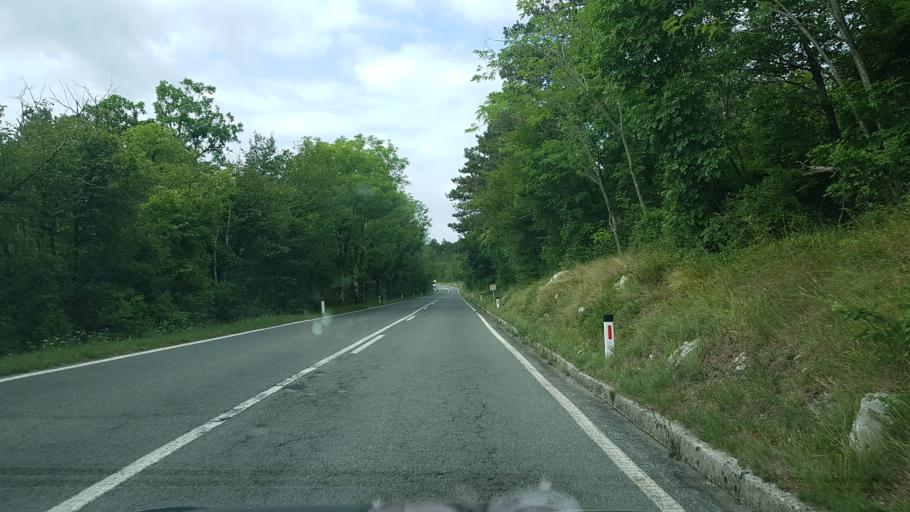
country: SI
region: Divaca
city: Divaca
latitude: 45.6661
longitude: 13.9440
